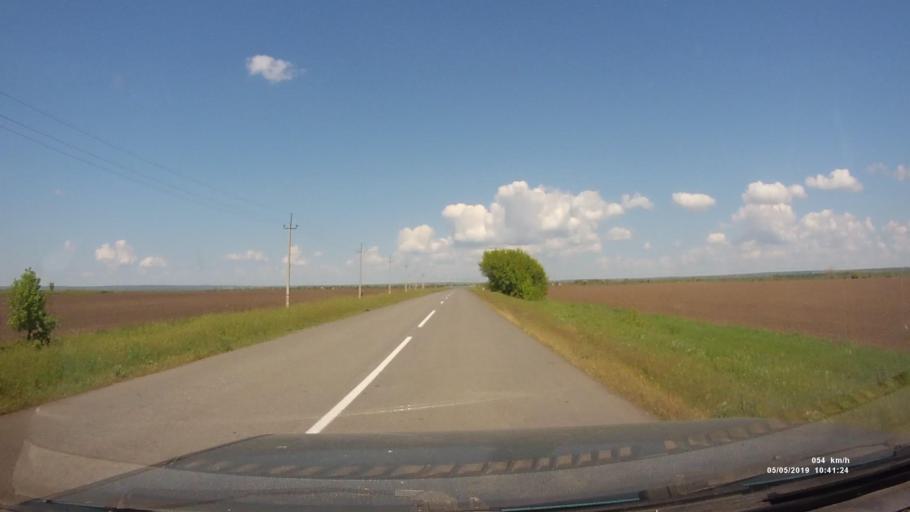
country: RU
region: Rostov
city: Ust'-Donetskiy
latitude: 47.5907
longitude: 40.8426
